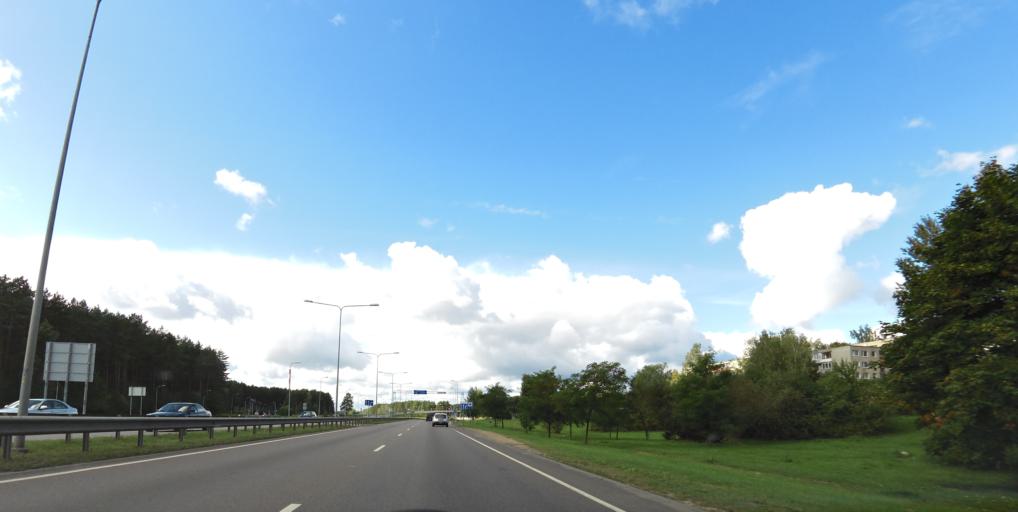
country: LT
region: Vilnius County
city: Lazdynai
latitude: 54.6706
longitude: 25.2051
